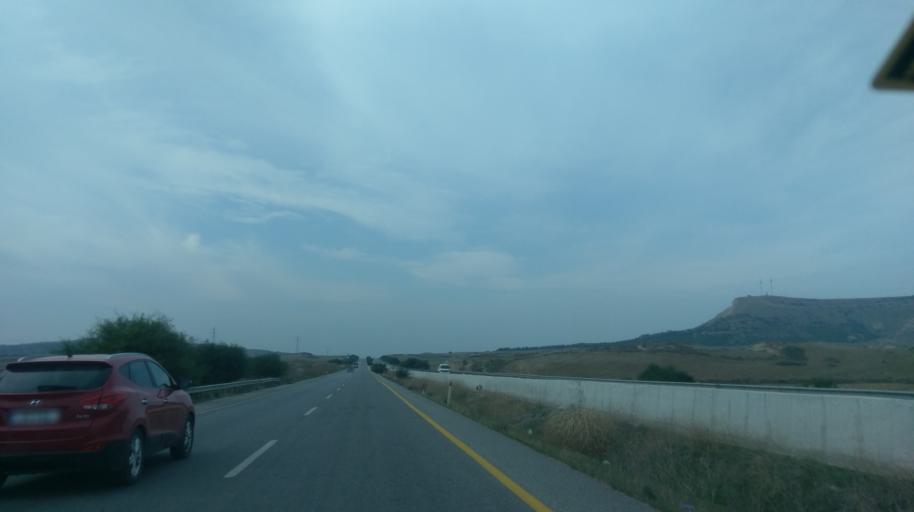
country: CY
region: Lefkosia
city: Mammari
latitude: 35.2201
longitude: 33.1465
